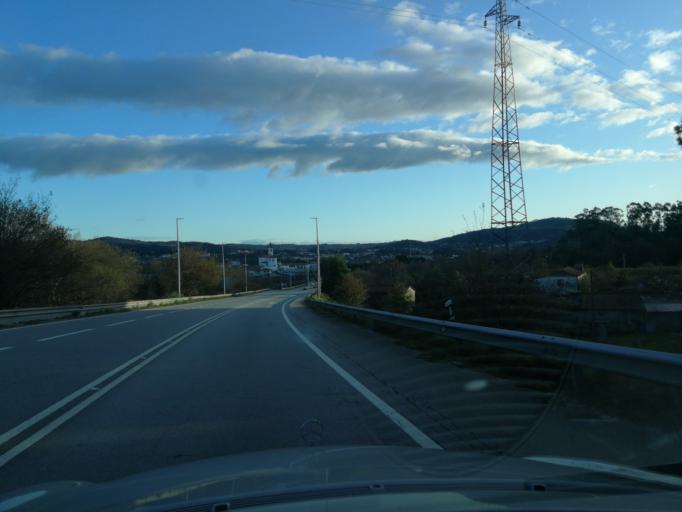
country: PT
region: Braga
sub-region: Barcelos
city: Vila Frescainha
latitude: 41.5382
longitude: -8.6390
